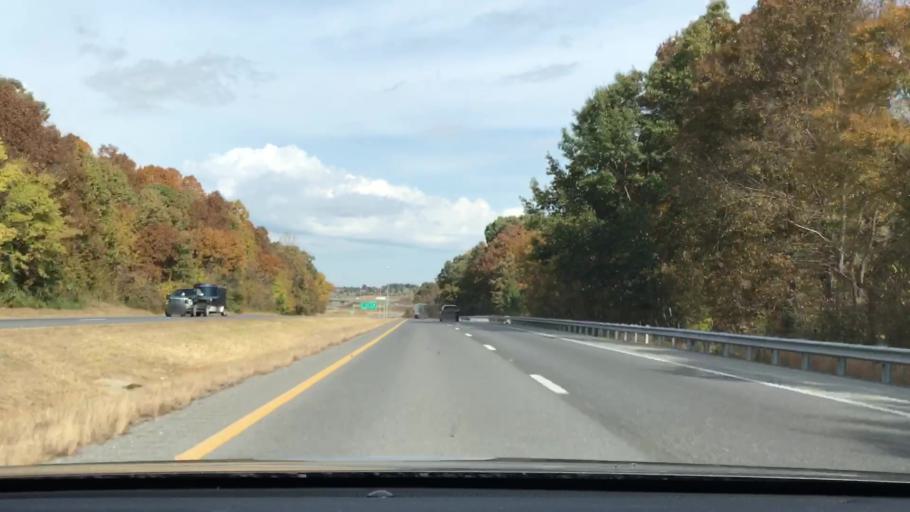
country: US
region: Kentucky
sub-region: Marshall County
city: Calvert City
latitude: 36.9743
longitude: -88.3460
